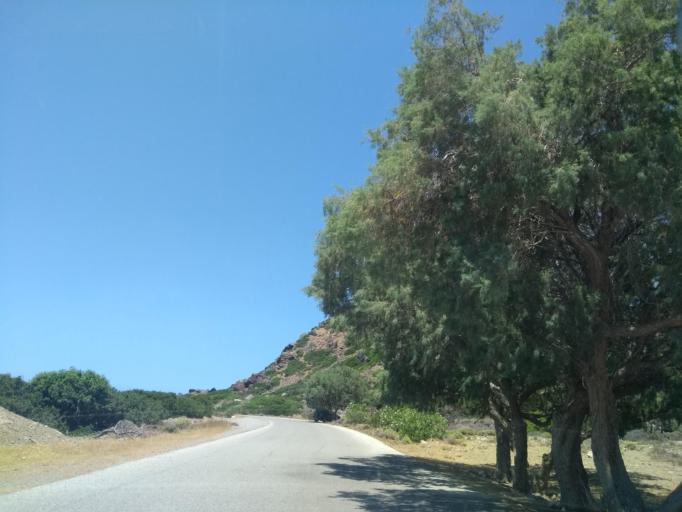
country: GR
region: Crete
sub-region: Nomos Chanias
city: Vryses
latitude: 35.3493
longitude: 23.5387
